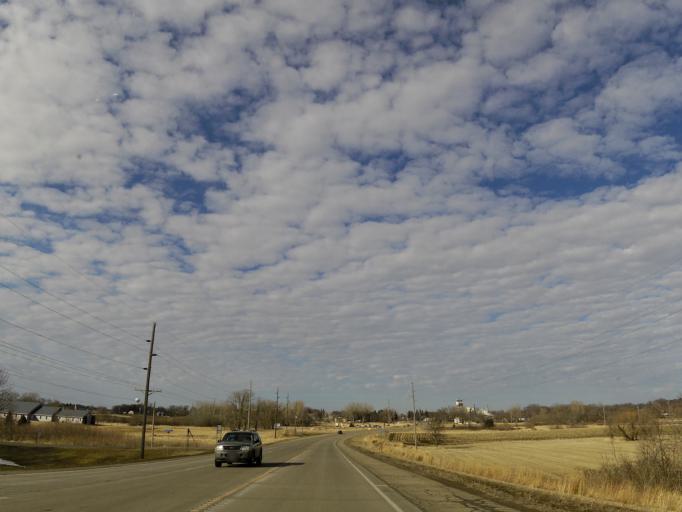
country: US
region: Minnesota
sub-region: Le Sueur County
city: New Prague
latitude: 44.5327
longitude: -93.5856
